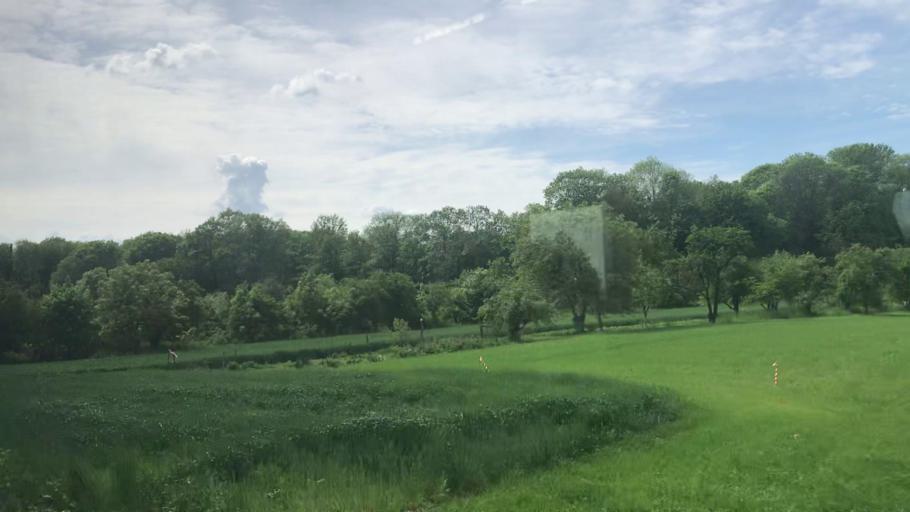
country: PL
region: Lower Silesian Voivodeship
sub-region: Powiat wroclawski
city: Katy Wroclawskie
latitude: 51.0056
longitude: 16.6945
